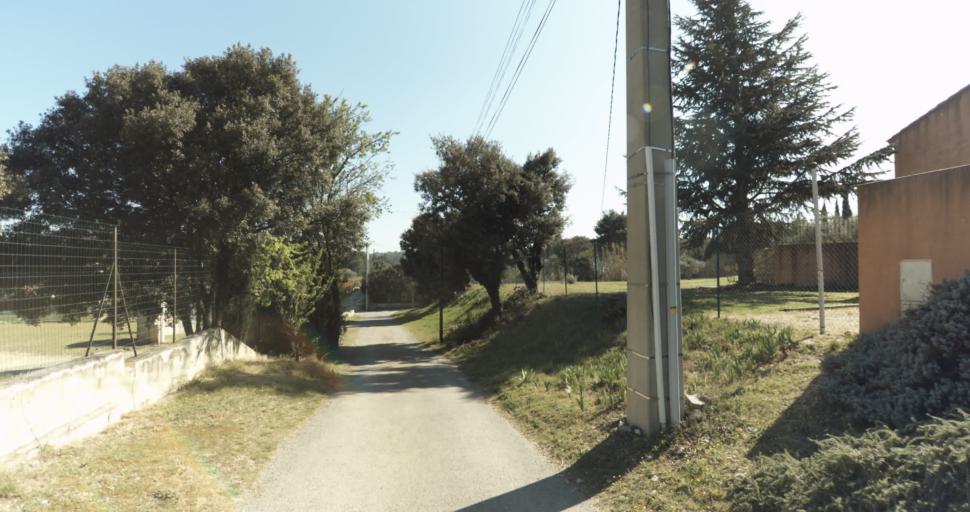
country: FR
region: Provence-Alpes-Cote d'Azur
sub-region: Departement des Bouches-du-Rhone
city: Pelissanne
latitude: 43.6433
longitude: 5.1599
